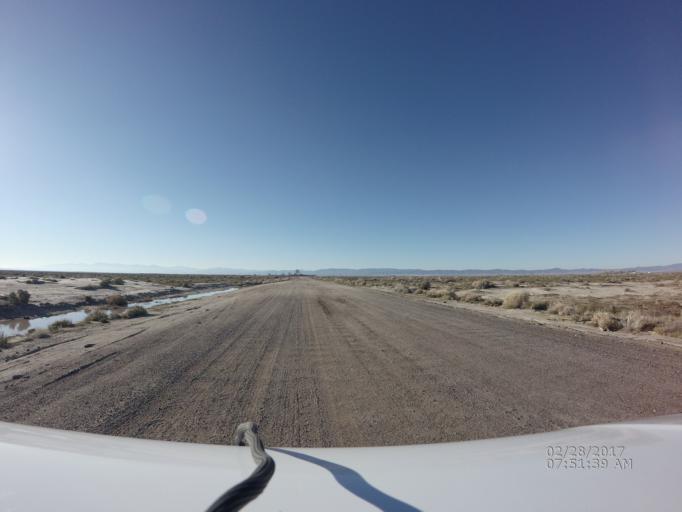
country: US
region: California
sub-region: Kern County
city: Rosamond
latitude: 34.8129
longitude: -118.1848
